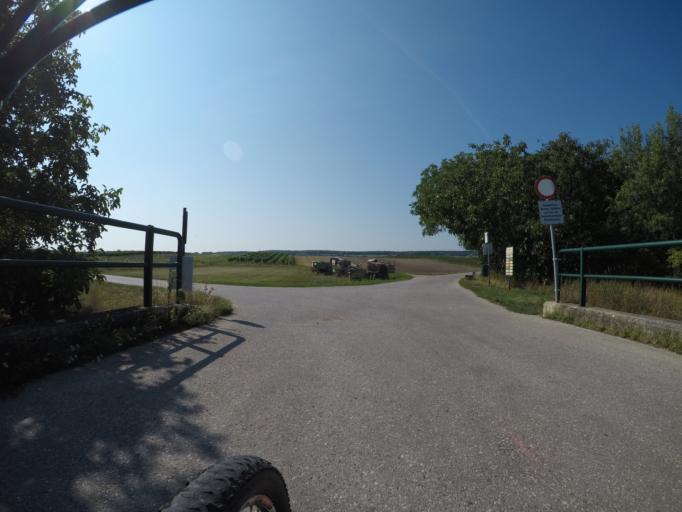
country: AT
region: Lower Austria
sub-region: Politischer Bezirk Baden
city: Bad Voslau
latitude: 47.9569
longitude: 16.1884
